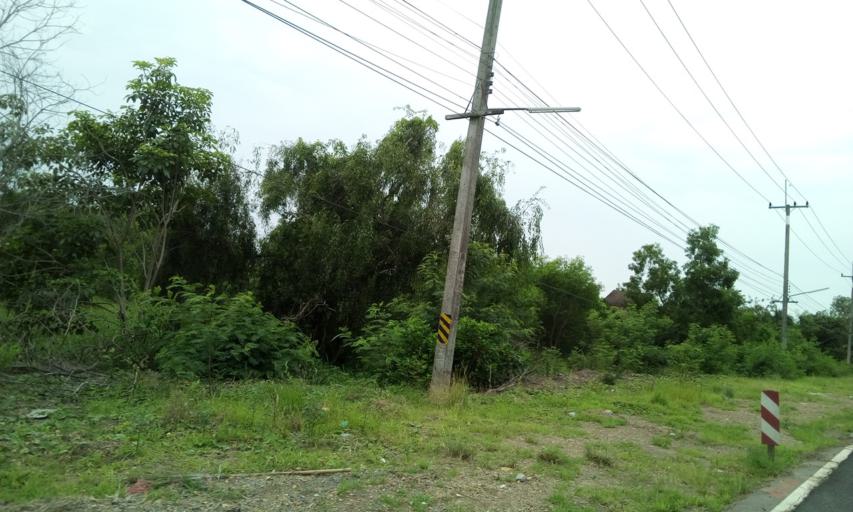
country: TH
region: Pathum Thani
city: Nong Suea
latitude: 14.2397
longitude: 100.8233
